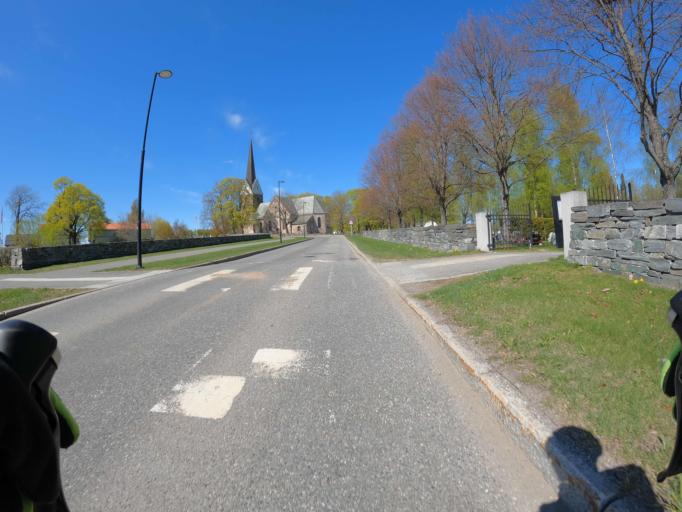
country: NO
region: Akershus
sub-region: Skedsmo
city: Lillestrom
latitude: 59.9928
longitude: 11.0468
